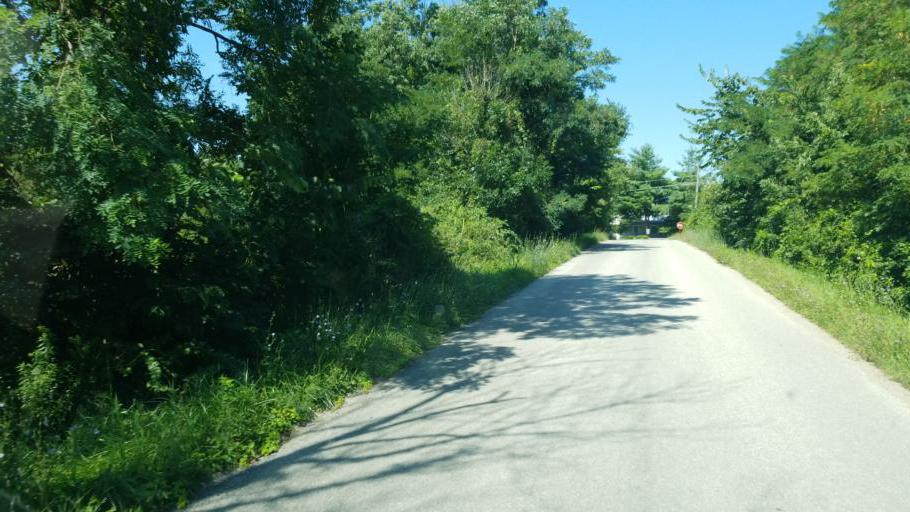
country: US
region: Ohio
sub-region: Morrow County
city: Cardington
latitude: 40.4334
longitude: -82.8328
